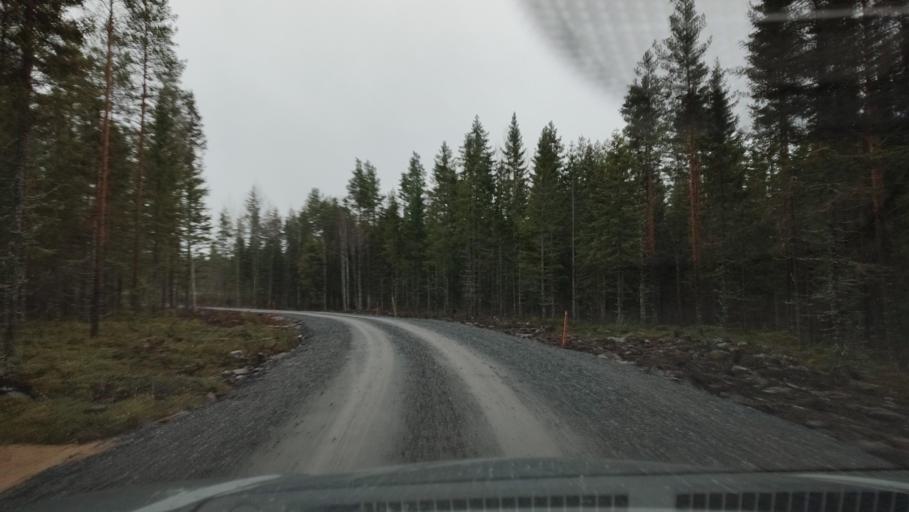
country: FI
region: Southern Ostrobothnia
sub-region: Suupohja
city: Karijoki
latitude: 62.1600
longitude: 21.5901
